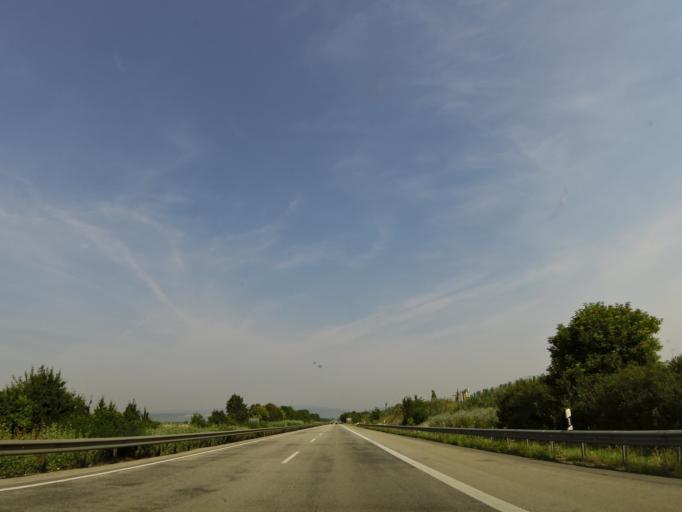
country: DE
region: Rheinland-Pfalz
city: Zotzenheim
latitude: 49.8573
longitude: 7.9728
